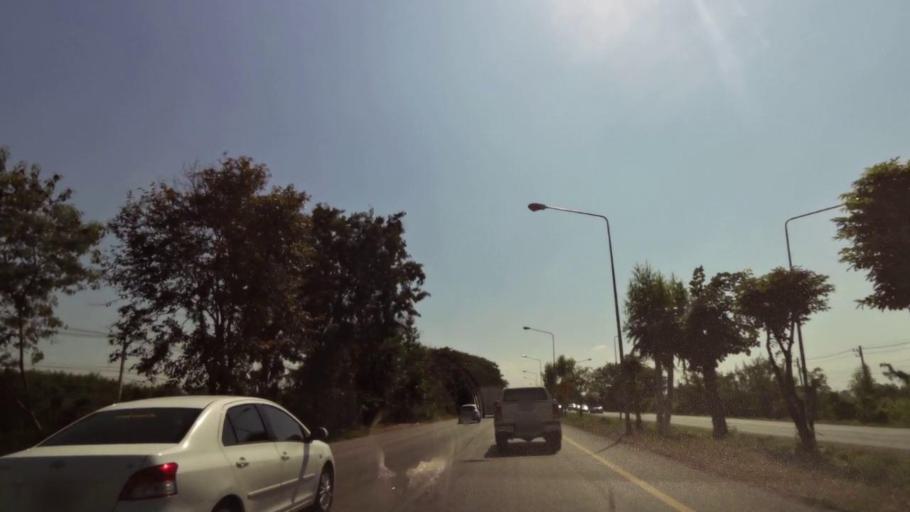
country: TH
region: Nakhon Sawan
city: Kao Liao
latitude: 15.8011
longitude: 100.1203
